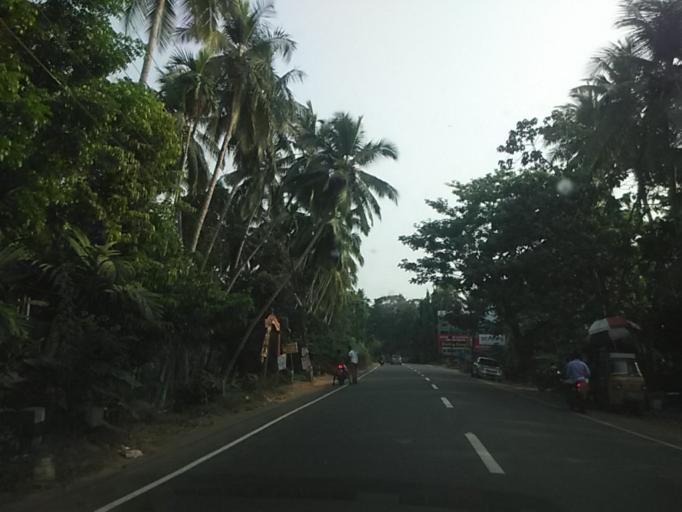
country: IN
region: Kerala
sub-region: Kozhikode
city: Kozhikode
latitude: 11.3444
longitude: 75.7616
